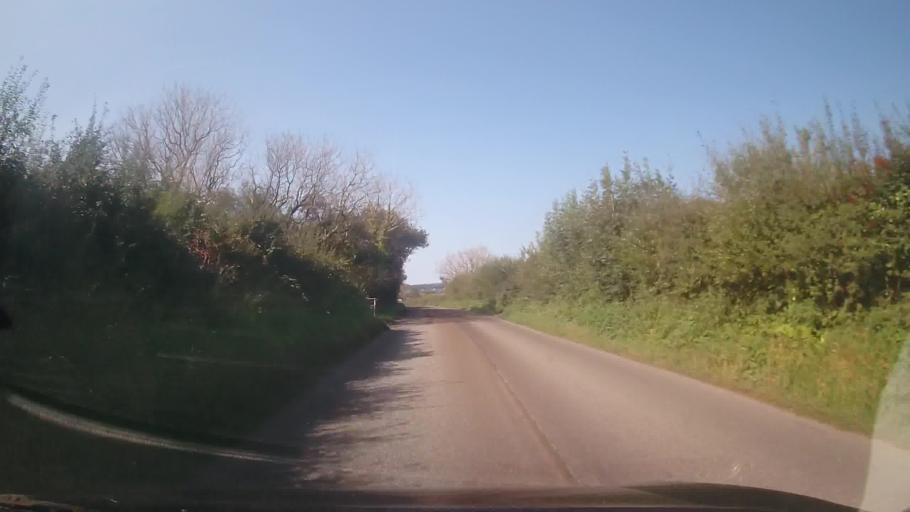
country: GB
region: Wales
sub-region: Pembrokeshire
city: Camrose
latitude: 51.8442
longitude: -5.0038
